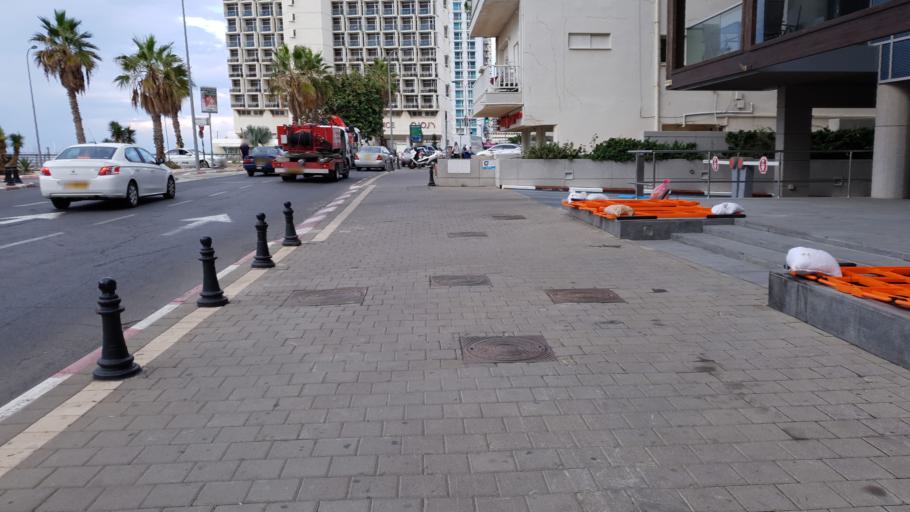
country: IL
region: Tel Aviv
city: Tel Aviv
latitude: 32.0818
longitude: 34.7685
